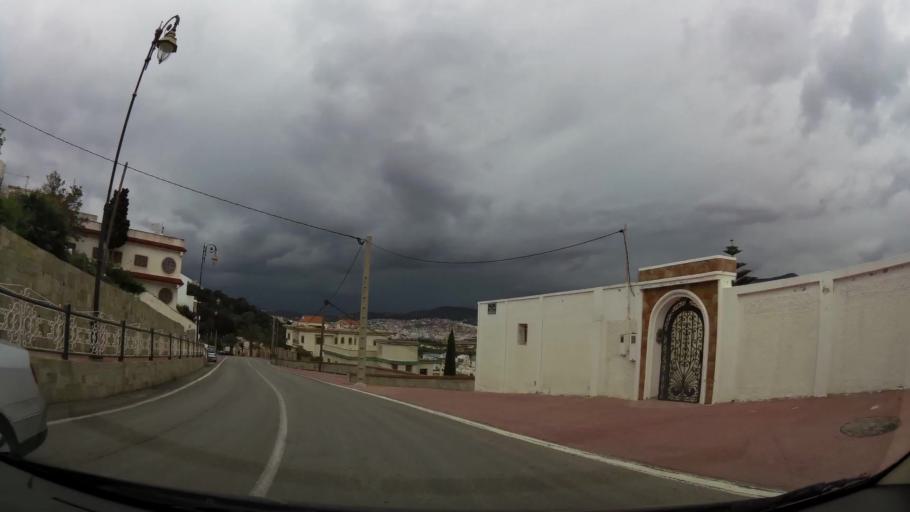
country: MA
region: Tanger-Tetouan
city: Tetouan
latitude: 35.5527
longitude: -5.3709
